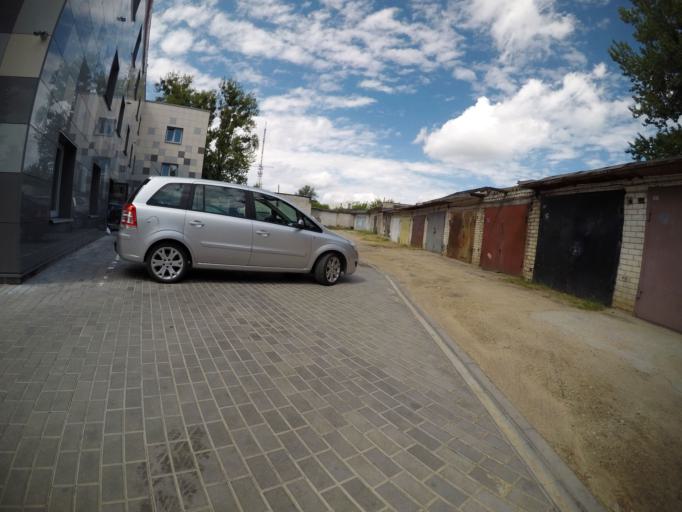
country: BY
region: Grodnenskaya
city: Hrodna
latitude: 53.6993
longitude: 23.8338
